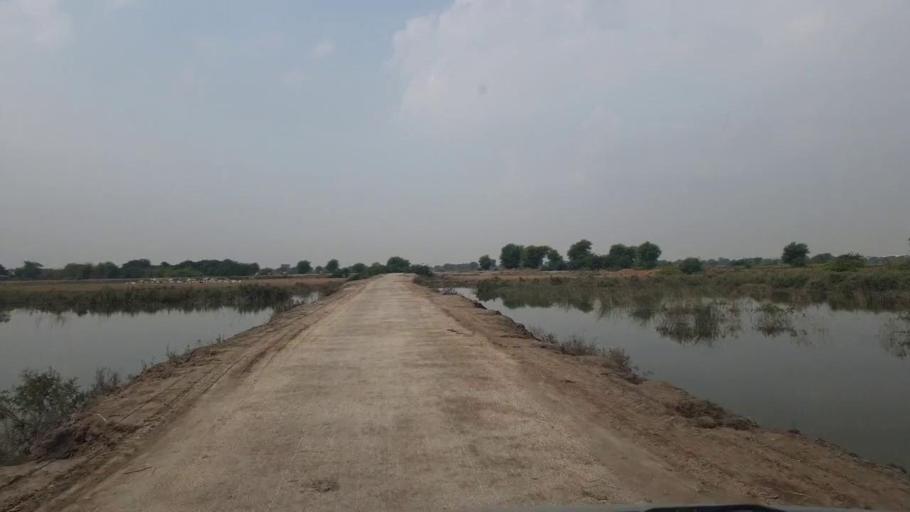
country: PK
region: Sindh
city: Talhar
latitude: 24.8615
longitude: 68.8283
